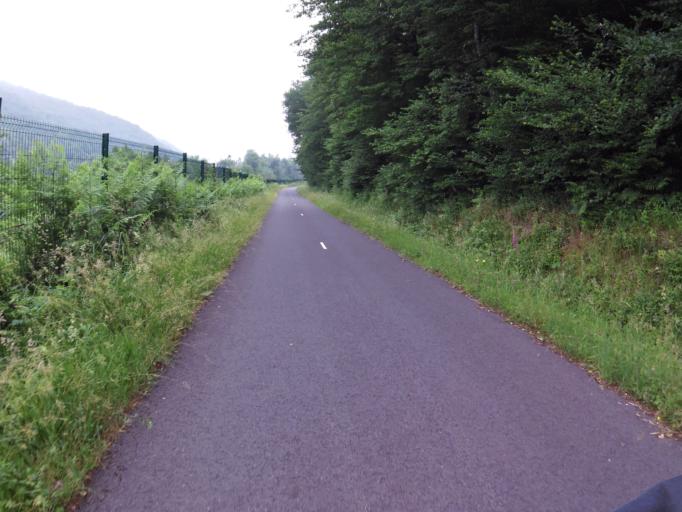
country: FR
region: Champagne-Ardenne
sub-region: Departement des Ardennes
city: Revin
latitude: 49.9571
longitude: 4.6574
